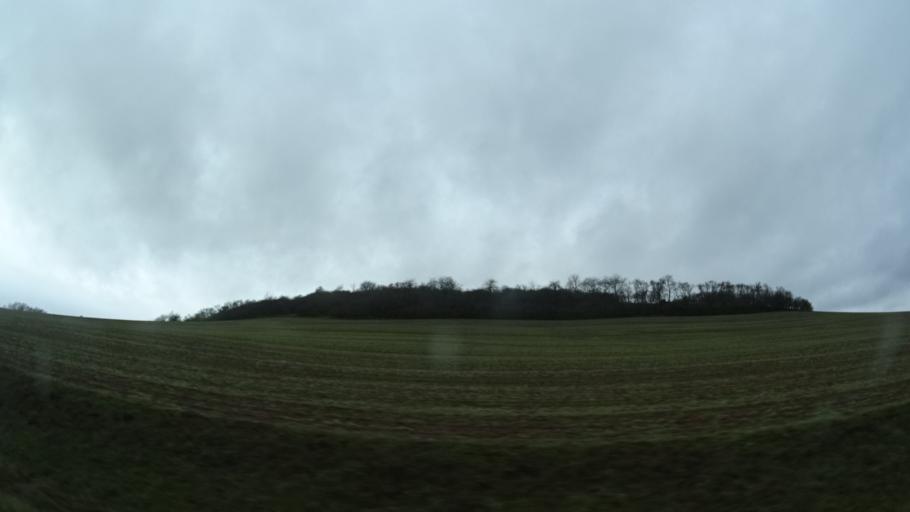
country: DE
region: Thuringia
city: Juchsen
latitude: 50.4735
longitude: 10.4895
